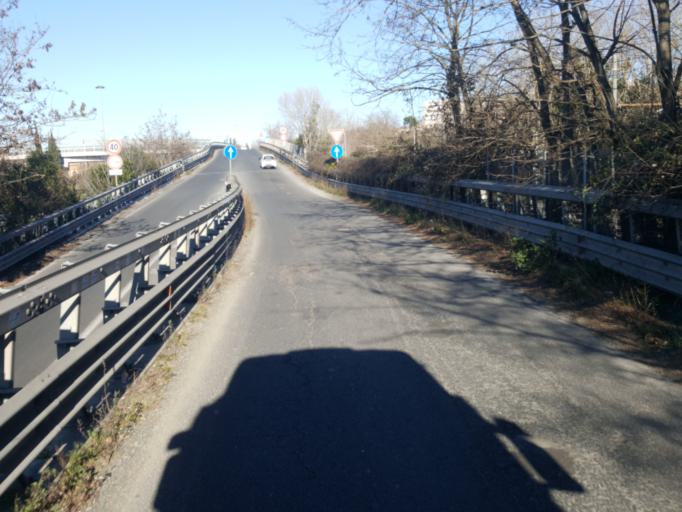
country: IT
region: Latium
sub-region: Citta metropolitana di Roma Capitale
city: Vitinia
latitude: 41.8017
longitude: 12.4184
